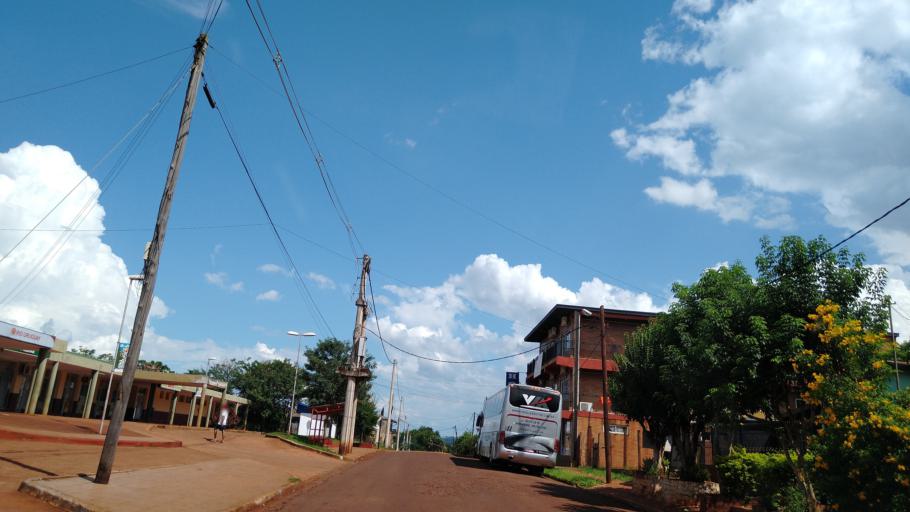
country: AR
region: Misiones
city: Puerto Libertad
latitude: -25.9681
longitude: -54.5716
